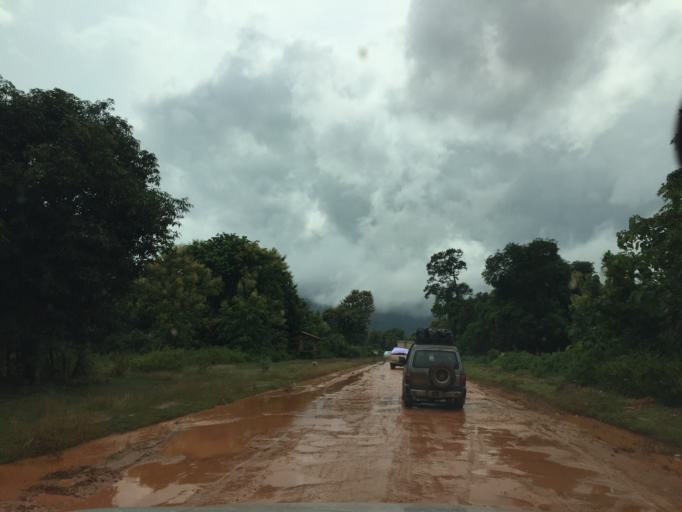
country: LA
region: Attapu
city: Attapu
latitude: 14.8077
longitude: 106.7680
